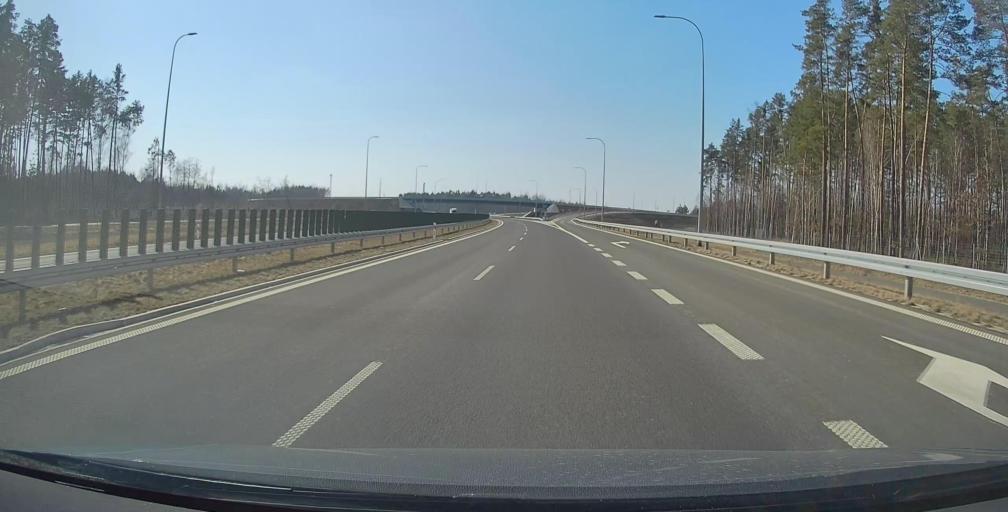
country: PL
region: Subcarpathian Voivodeship
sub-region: Powiat nizanski
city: Jarocin
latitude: 50.6469
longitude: 22.2912
